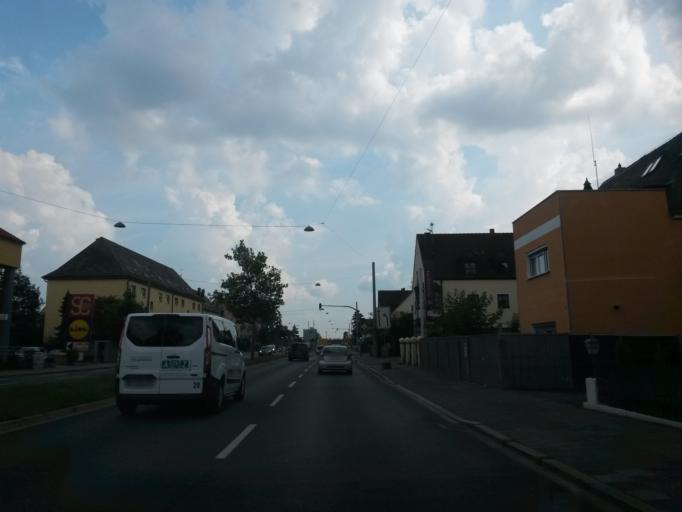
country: DE
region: Bavaria
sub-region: Regierungsbezirk Mittelfranken
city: Furth
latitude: 49.4564
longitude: 10.9885
